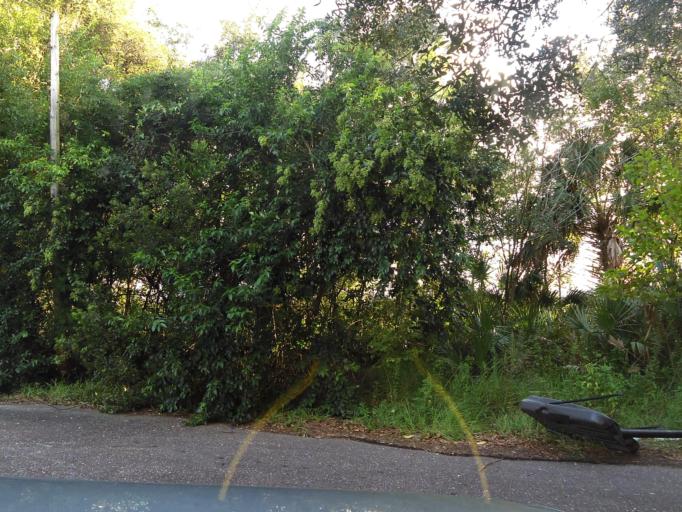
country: US
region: Florida
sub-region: Duval County
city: Jacksonville
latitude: 30.3502
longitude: -81.7050
